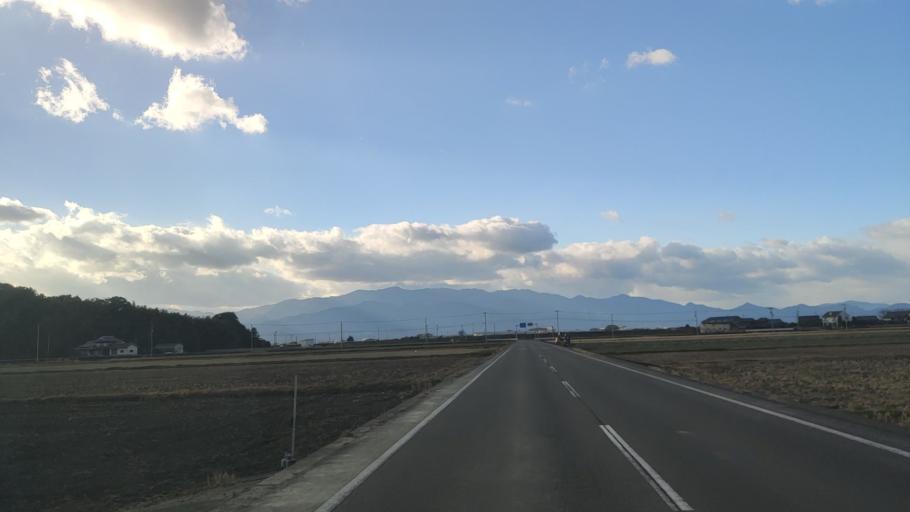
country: JP
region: Ehime
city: Saijo
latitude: 33.9039
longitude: 133.1325
